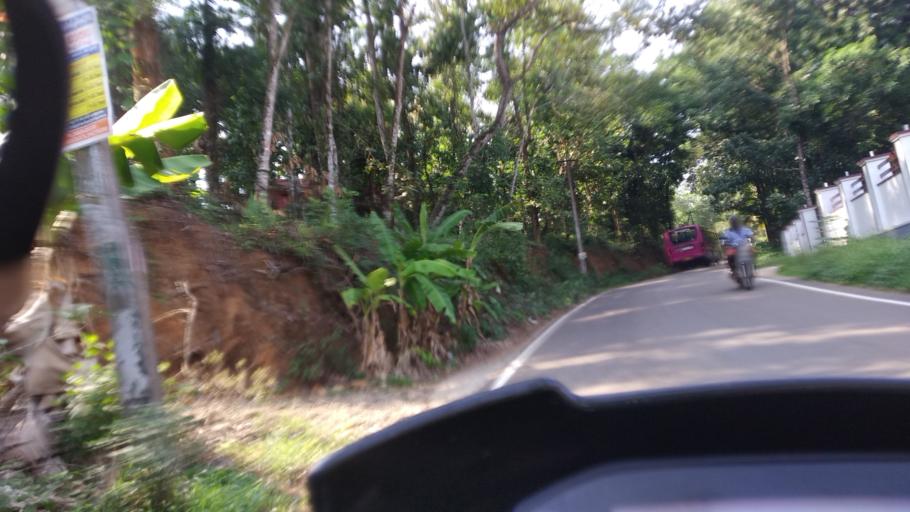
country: IN
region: Kerala
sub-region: Ernakulam
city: Piravam
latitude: 9.8137
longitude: 76.5609
